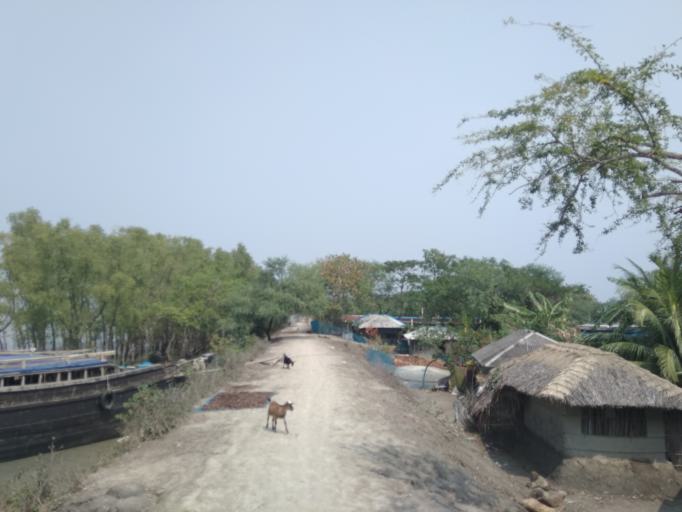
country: IN
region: West Bengal
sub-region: North 24 Parganas
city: Gosaba
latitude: 22.2472
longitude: 89.2497
